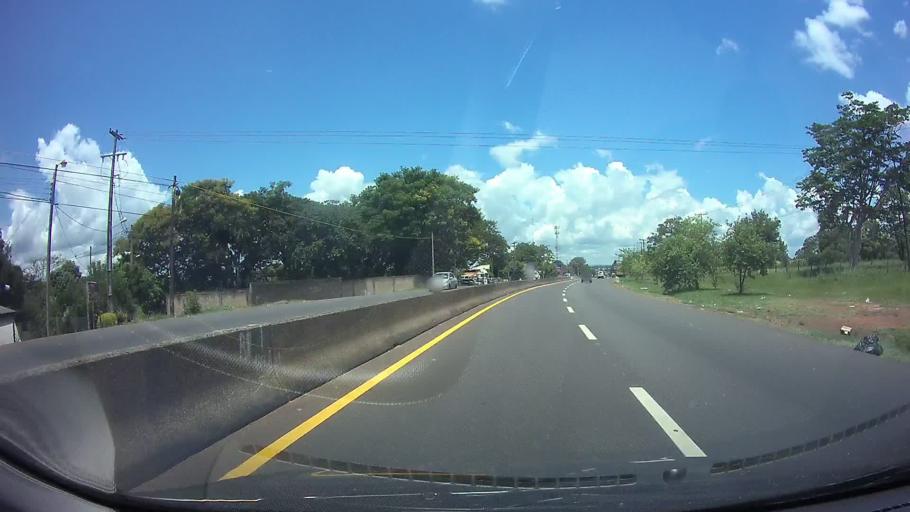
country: PY
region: Central
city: Itaugua
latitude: -25.3793
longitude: -57.3809
